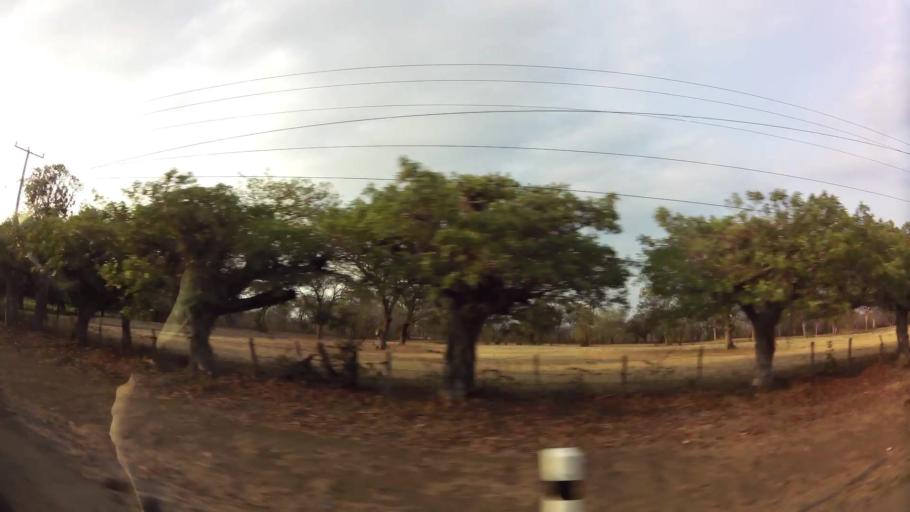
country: NI
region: Leon
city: Nagarote
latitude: 12.2725
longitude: -86.4900
